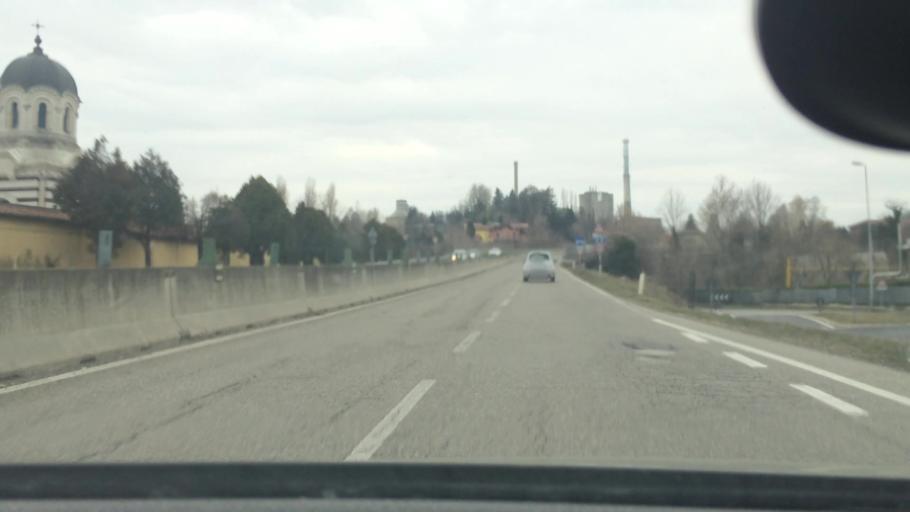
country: IT
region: Lombardy
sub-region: Provincia di Como
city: Merone
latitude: 45.7881
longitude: 9.2425
